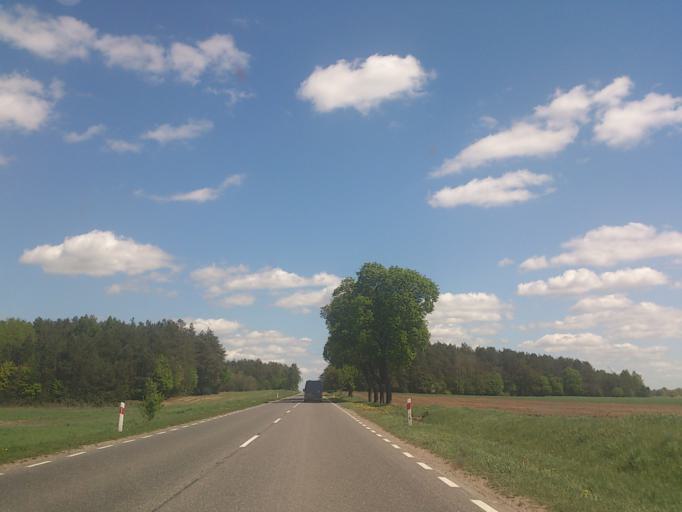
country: PL
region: Podlasie
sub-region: Lomza
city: Lomza
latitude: 53.1647
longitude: 21.9662
